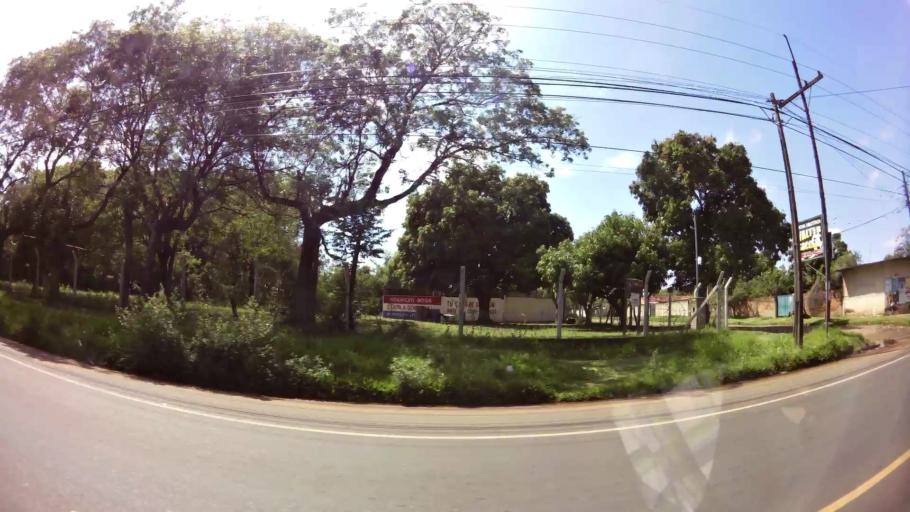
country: PY
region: Central
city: San Lorenzo
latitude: -25.2809
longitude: -57.4983
